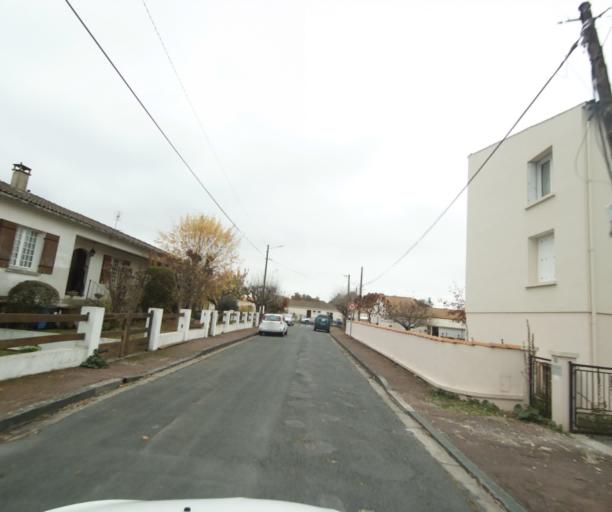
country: FR
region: Poitou-Charentes
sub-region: Departement de la Charente-Maritime
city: Saintes
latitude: 45.7356
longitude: -0.6204
